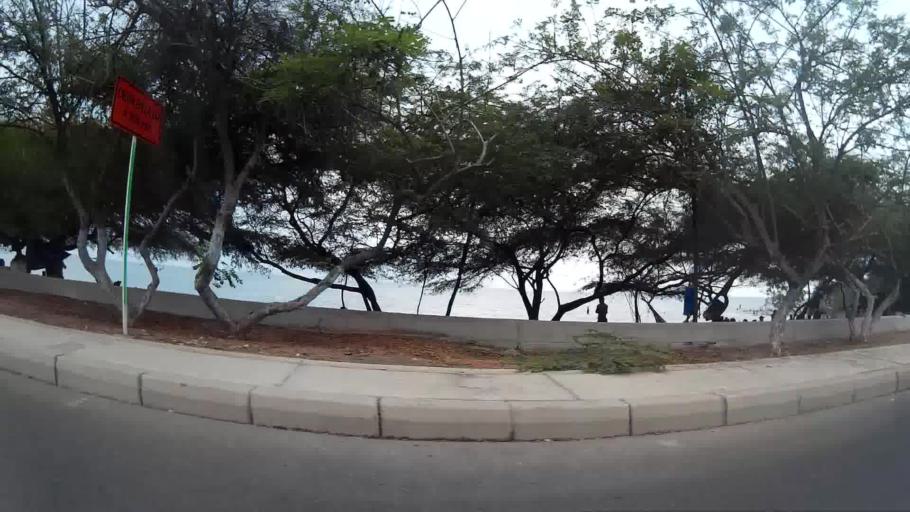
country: CO
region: Magdalena
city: Cienaga
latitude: 11.1202
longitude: -74.2319
